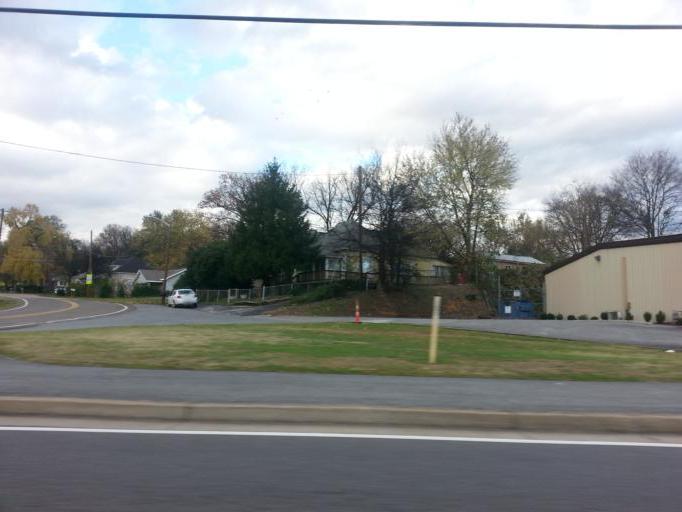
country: US
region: Tennessee
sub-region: Knox County
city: Knoxville
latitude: 35.9641
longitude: -83.9577
